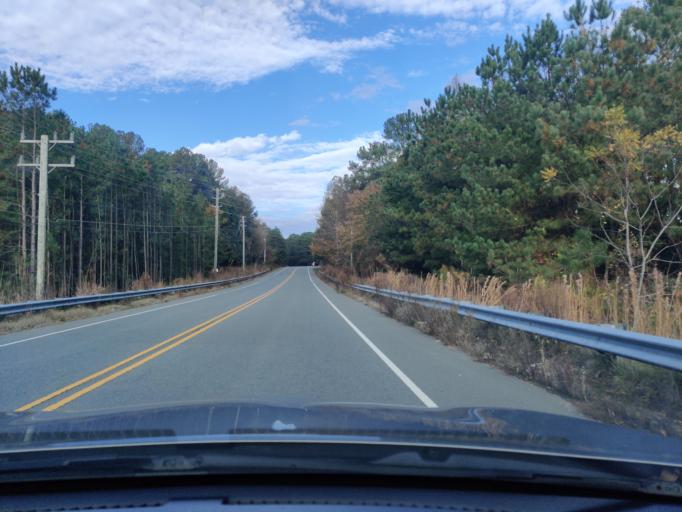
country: US
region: North Carolina
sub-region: Wake County
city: West Raleigh
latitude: 35.9155
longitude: -78.7091
